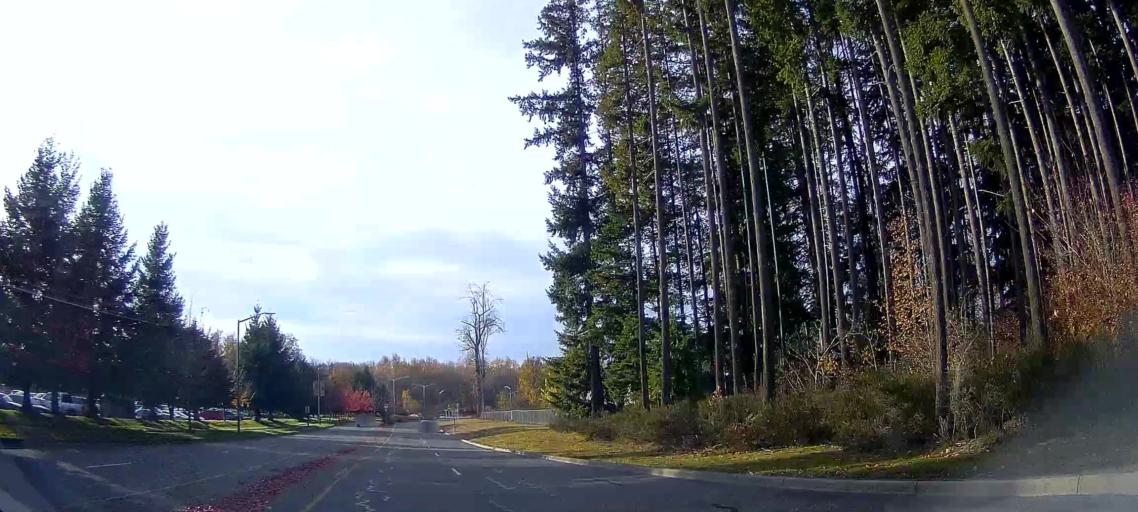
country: US
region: Washington
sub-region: Snohomish County
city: Marysville
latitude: 48.0960
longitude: -122.1869
